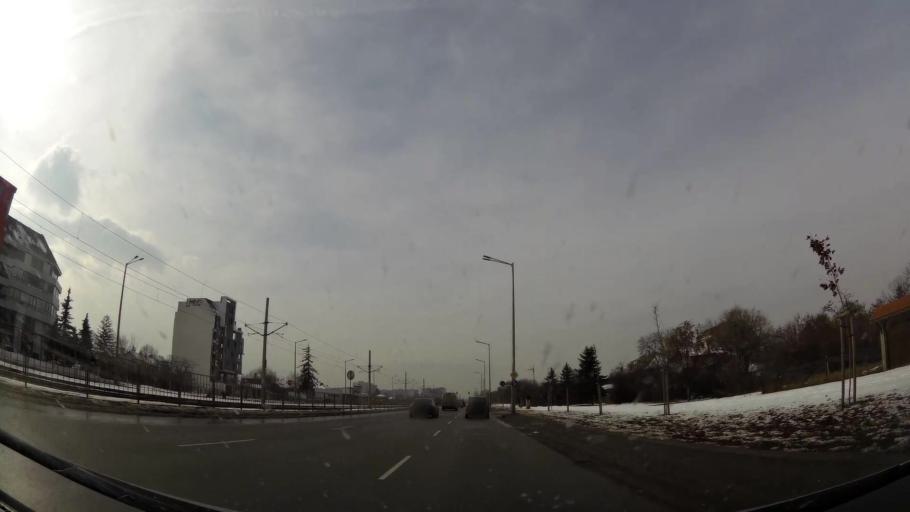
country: BG
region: Sofia-Capital
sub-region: Stolichna Obshtina
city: Sofia
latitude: 42.7023
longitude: 23.3811
